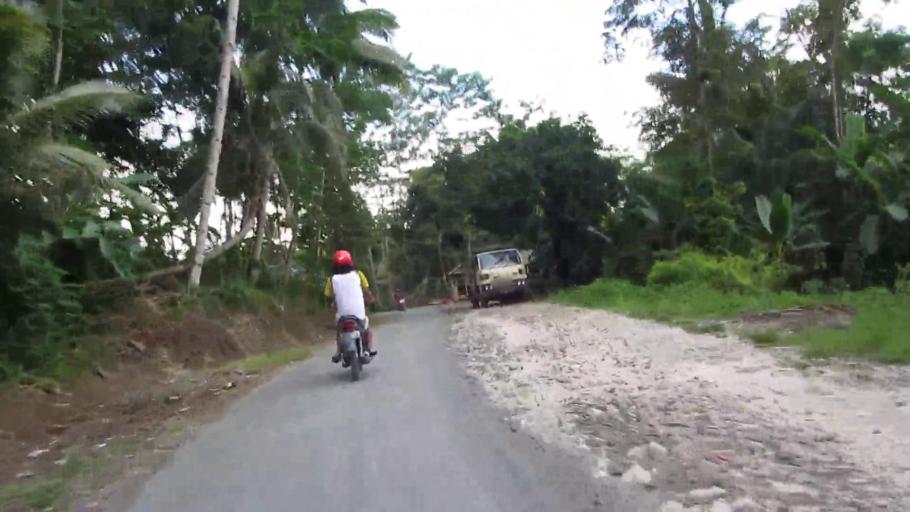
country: ID
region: West Java
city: Mandala
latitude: -7.7358
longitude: 108.4744
